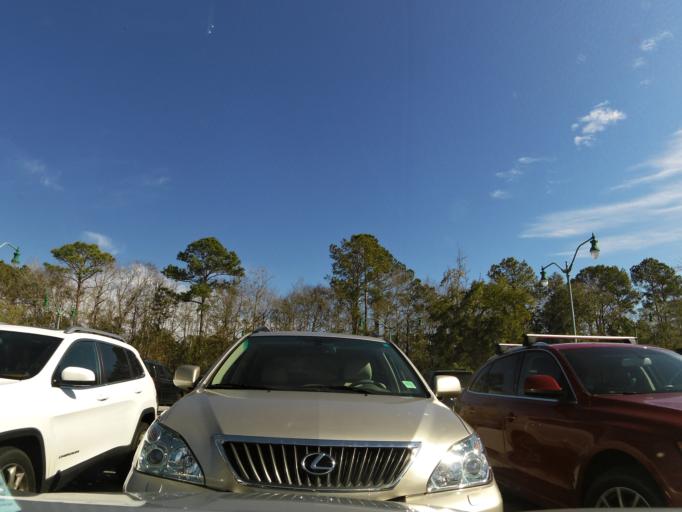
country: US
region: South Carolina
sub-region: Charleston County
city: Isle of Palms
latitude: 32.8239
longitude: -79.8177
